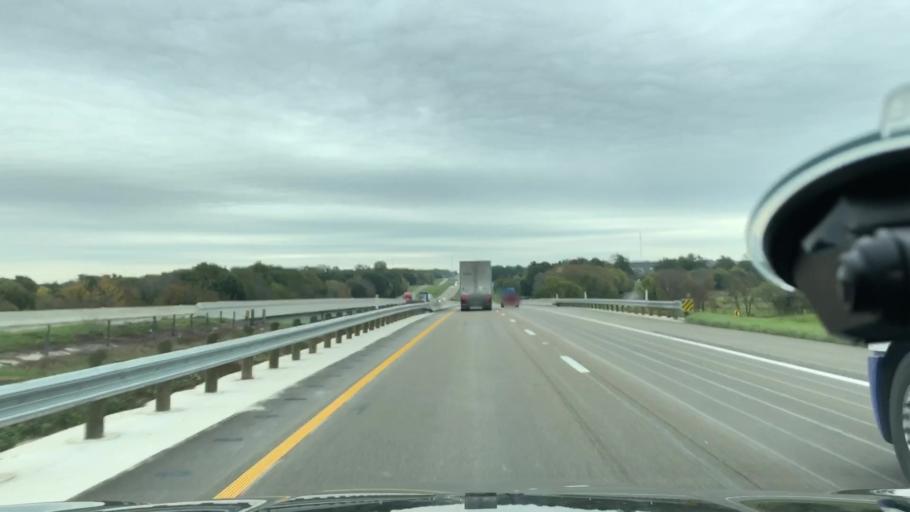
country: US
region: Texas
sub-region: Titus County
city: Mount Pleasant
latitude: 33.1633
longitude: -95.0203
